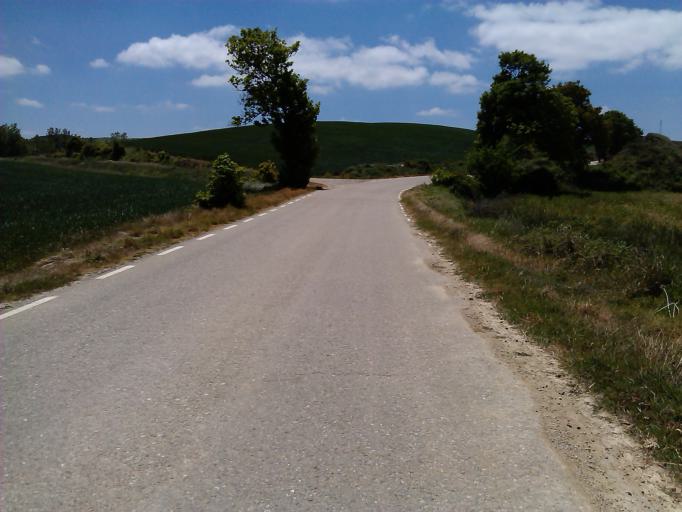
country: ES
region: Castille and Leon
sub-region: Provincia de Burgos
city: Cerraton de Juarros
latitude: 42.4361
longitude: -3.3528
